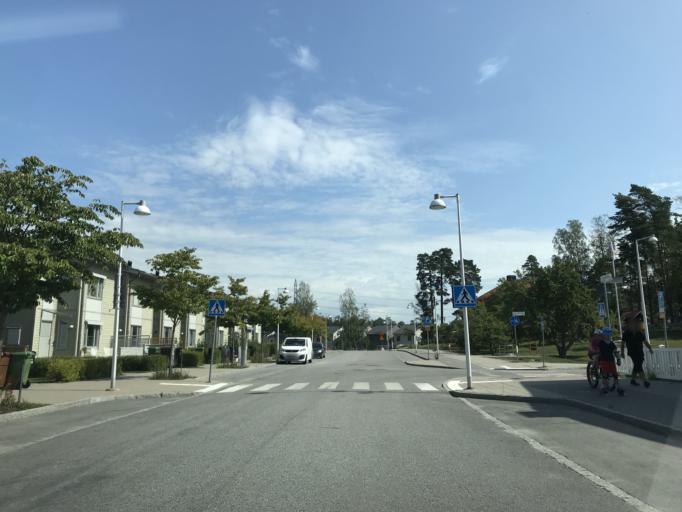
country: SE
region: Stockholm
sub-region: Solna Kommun
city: Rasunda
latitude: 59.3856
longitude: 17.9822
